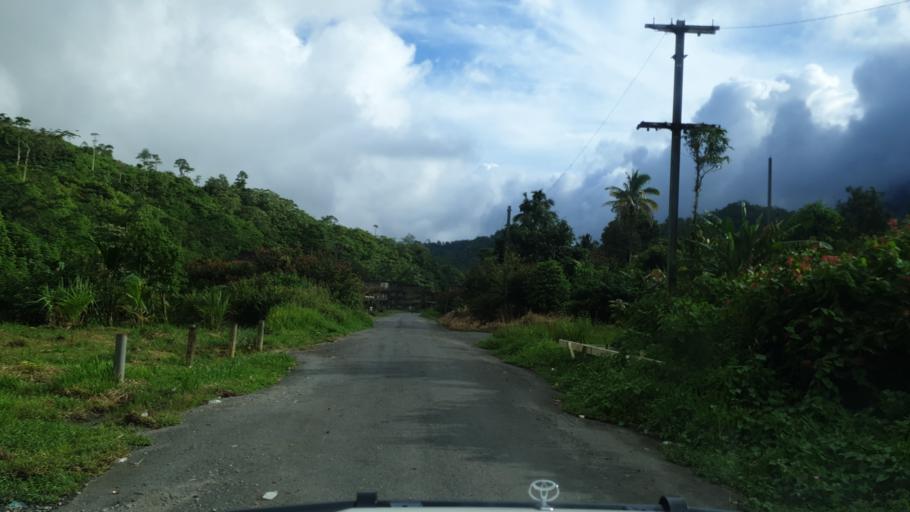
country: PG
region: Bougainville
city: Panguna
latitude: -6.3014
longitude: 155.4922
